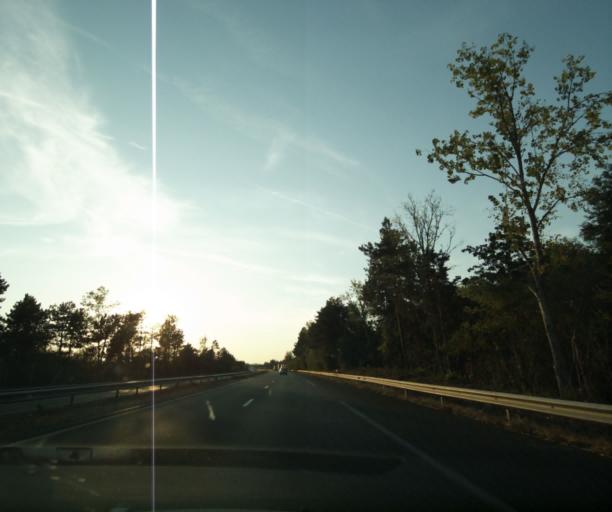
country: FR
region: Aquitaine
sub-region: Departement du Lot-et-Garonne
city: Roquefort
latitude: 44.1840
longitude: 0.5552
